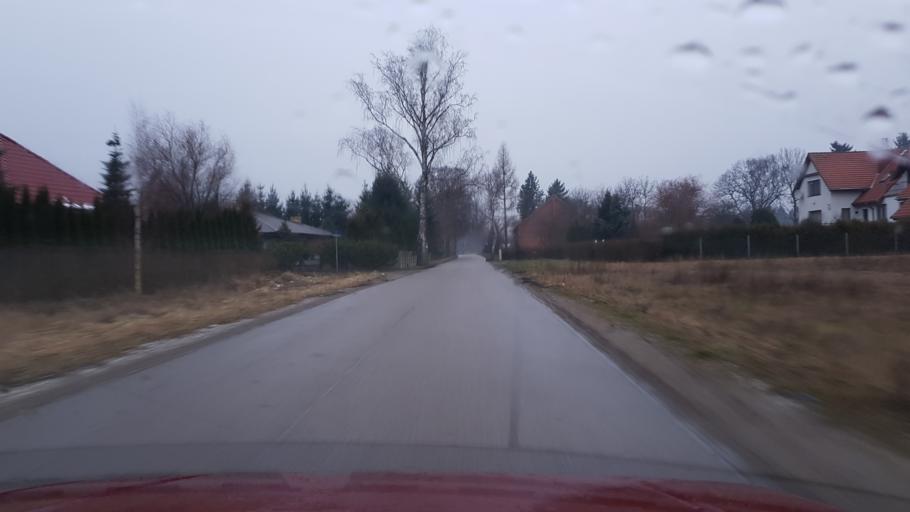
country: PL
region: West Pomeranian Voivodeship
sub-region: Koszalin
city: Koszalin
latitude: 54.1765
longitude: 16.2301
